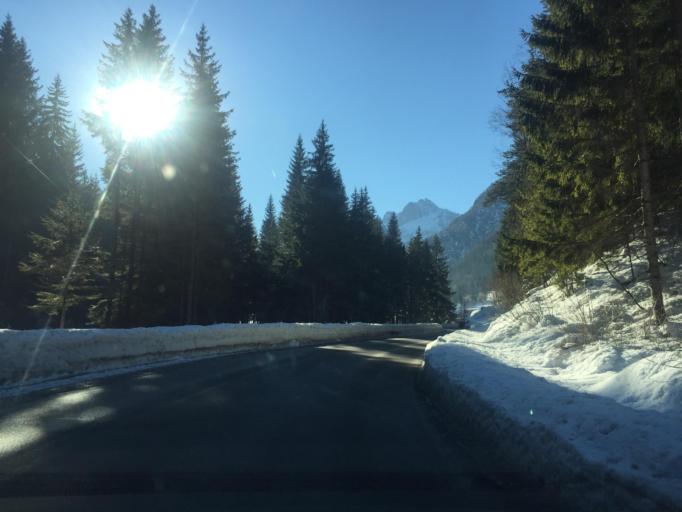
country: IT
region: Friuli Venezia Giulia
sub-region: Provincia di Udine
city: Malborghetto
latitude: 46.5045
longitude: 13.4849
